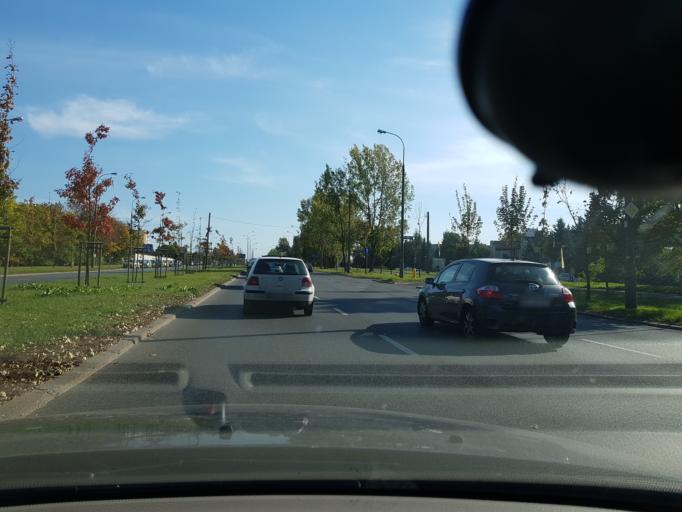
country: PL
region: Masovian Voivodeship
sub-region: Warszawa
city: Ursynow
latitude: 52.1657
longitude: 21.0347
